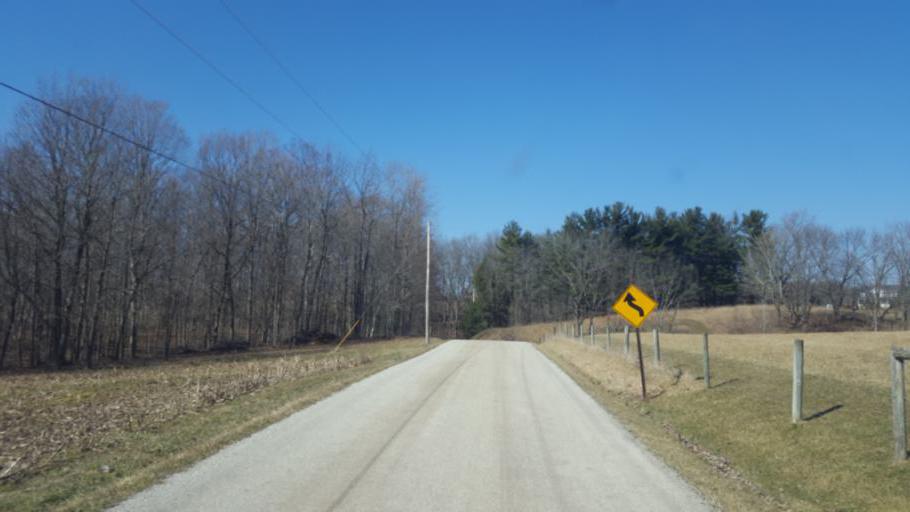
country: US
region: Ohio
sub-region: Richland County
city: Lincoln Heights
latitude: 40.8814
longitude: -82.4589
